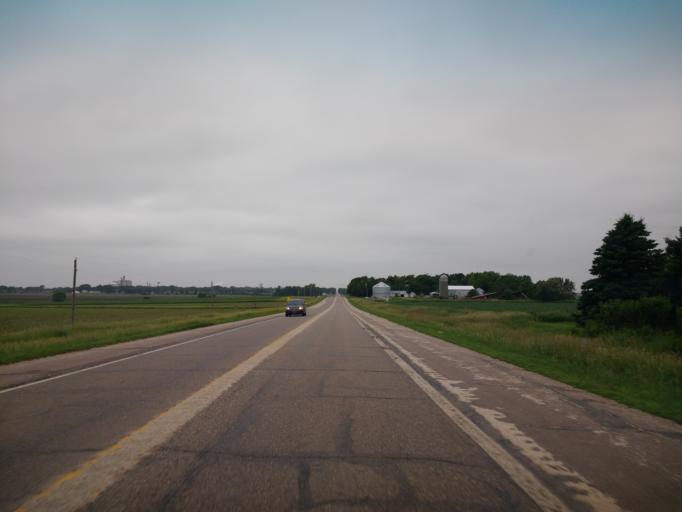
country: US
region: Iowa
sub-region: O'Brien County
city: Hartley
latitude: 43.1847
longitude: -95.4485
